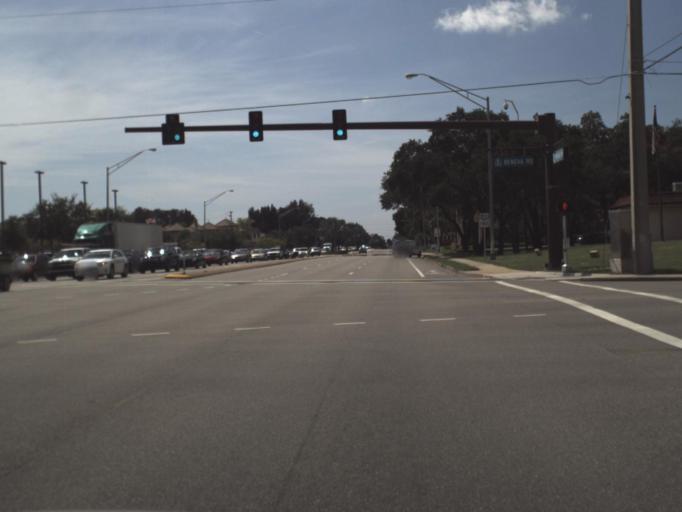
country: US
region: Florida
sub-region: Sarasota County
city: Kensington Park
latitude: 27.3376
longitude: -82.4972
